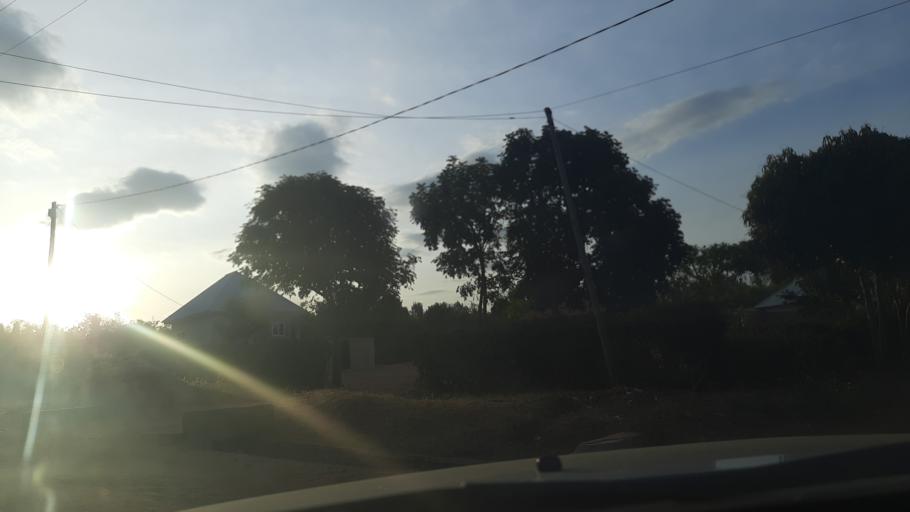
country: TZ
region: Singida
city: Singida
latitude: -4.8151
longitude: 34.7306
